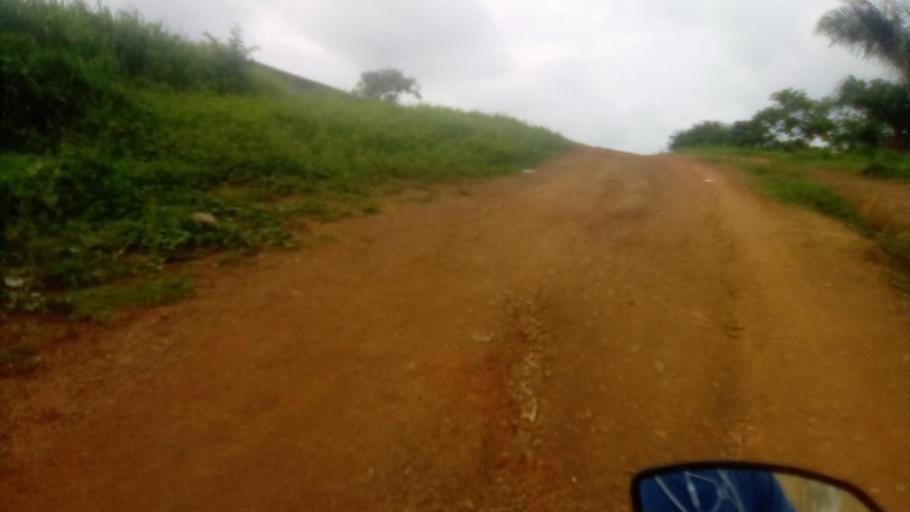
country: SL
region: Eastern Province
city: Kailahun
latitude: 8.2741
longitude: -10.5683
